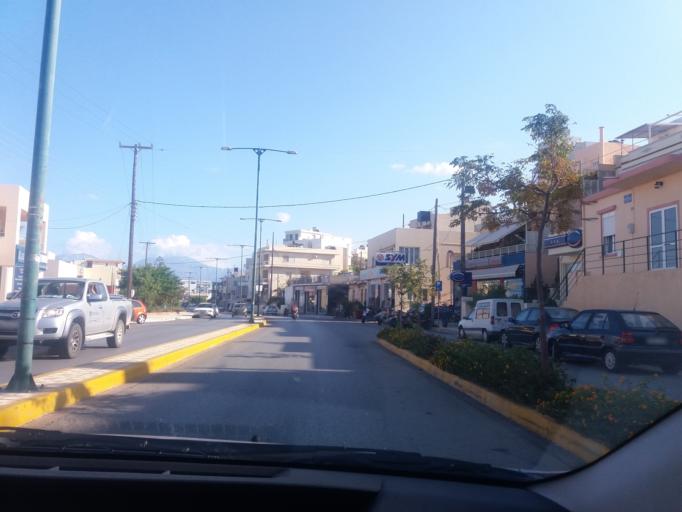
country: GR
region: Crete
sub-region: Nomos Lasithiou
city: Agios Nikolaos
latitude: 35.1970
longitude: 25.7110
